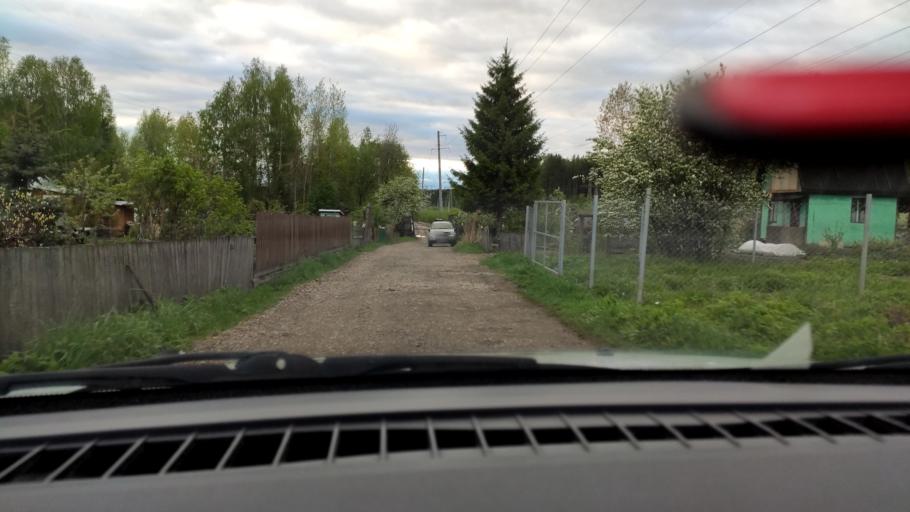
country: RU
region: Perm
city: Polazna
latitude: 58.1328
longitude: 56.4109
